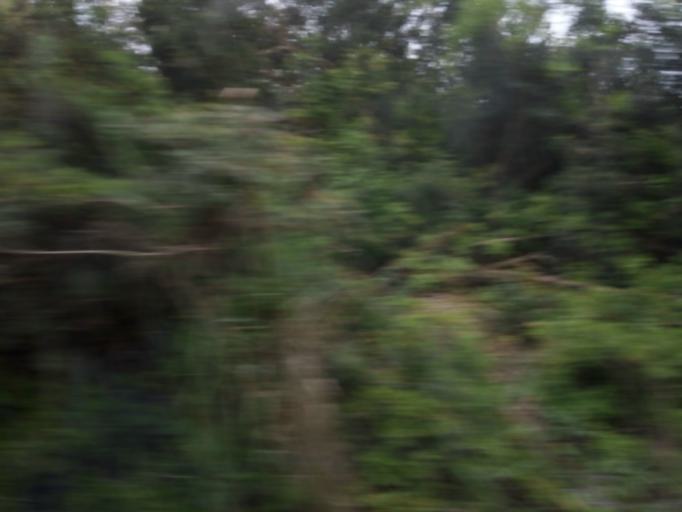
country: DZ
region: Tipaza
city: Tipasa
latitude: 36.5802
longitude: 2.5423
